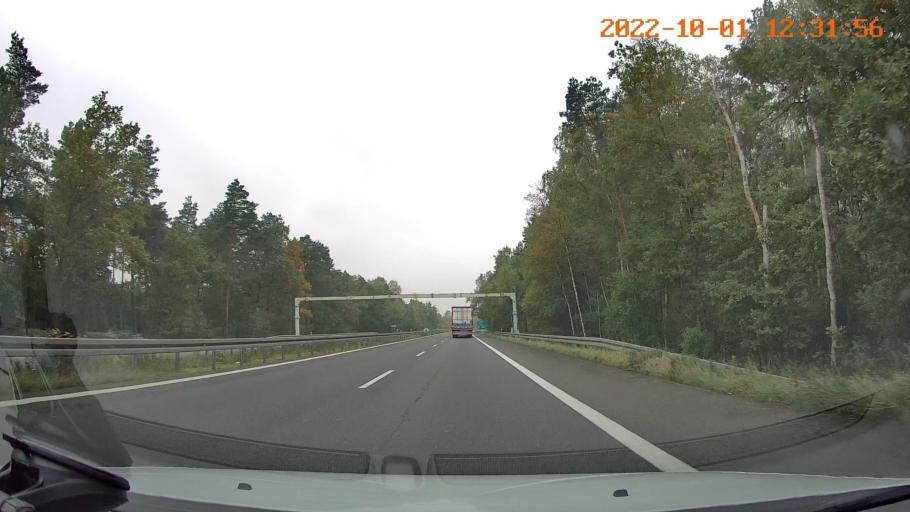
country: PL
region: Silesian Voivodeship
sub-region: Powiat bierunsko-ledzinski
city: Ledziny
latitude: 50.1609
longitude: 19.1506
